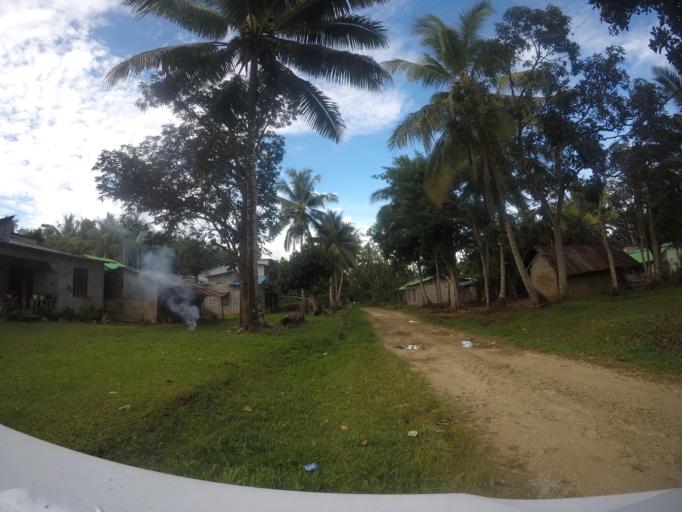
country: TL
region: Lautem
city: Lospalos
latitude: -8.5012
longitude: 126.9948
